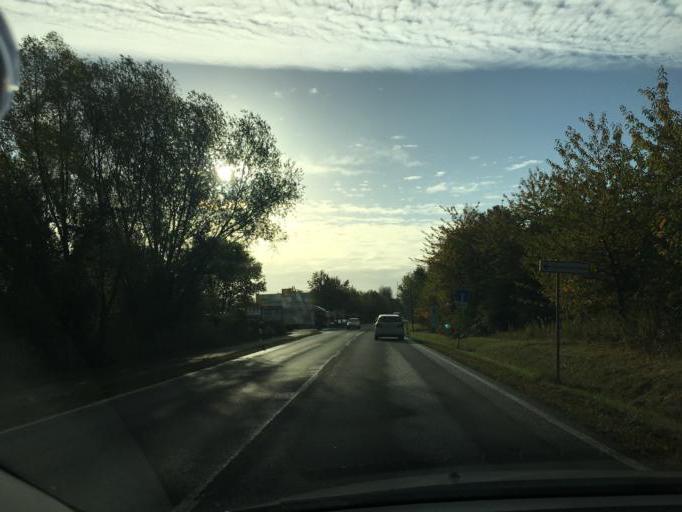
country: DE
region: Saxony
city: Borna
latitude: 51.1267
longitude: 12.4810
